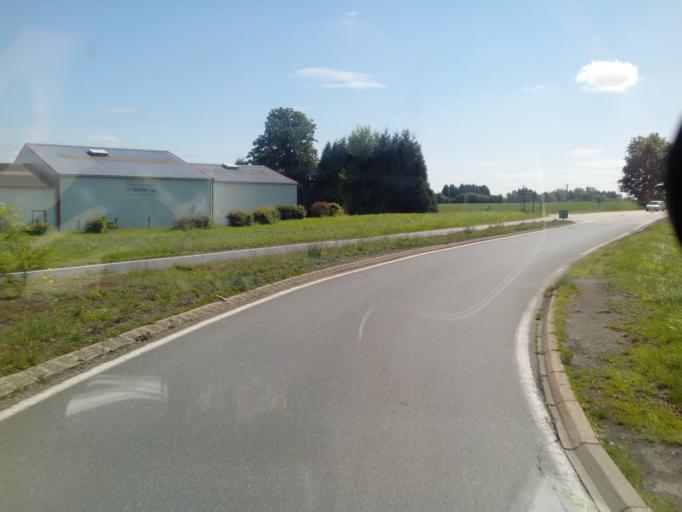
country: FR
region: Haute-Normandie
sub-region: Departement de l'Eure
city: Beuzeville
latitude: 49.3584
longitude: 0.3939
